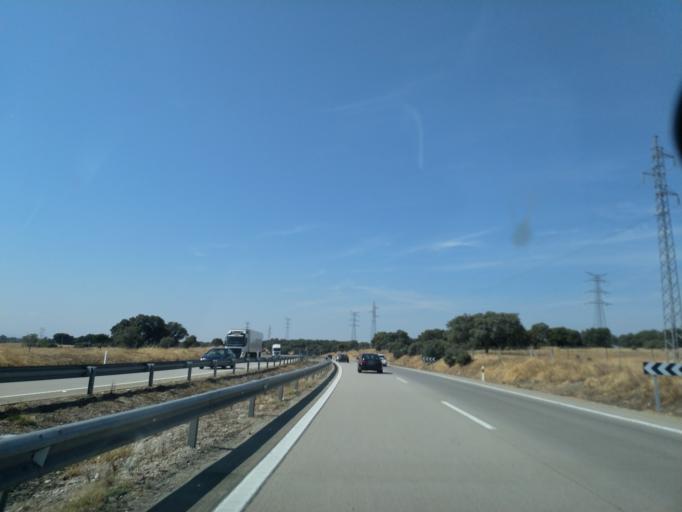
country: ES
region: Castille-La Mancha
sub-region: Province of Toledo
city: Mejorada
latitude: 39.9729
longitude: -4.8876
